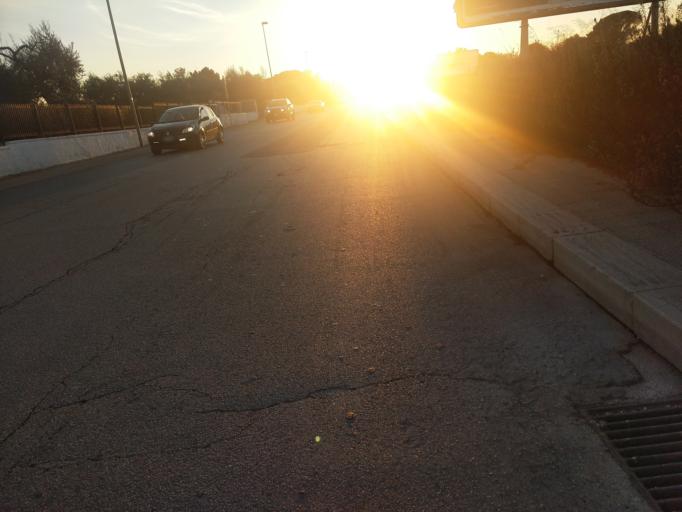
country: IT
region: Apulia
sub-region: Provincia di Bari
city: Modugno
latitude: 41.0844
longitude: 16.7998
